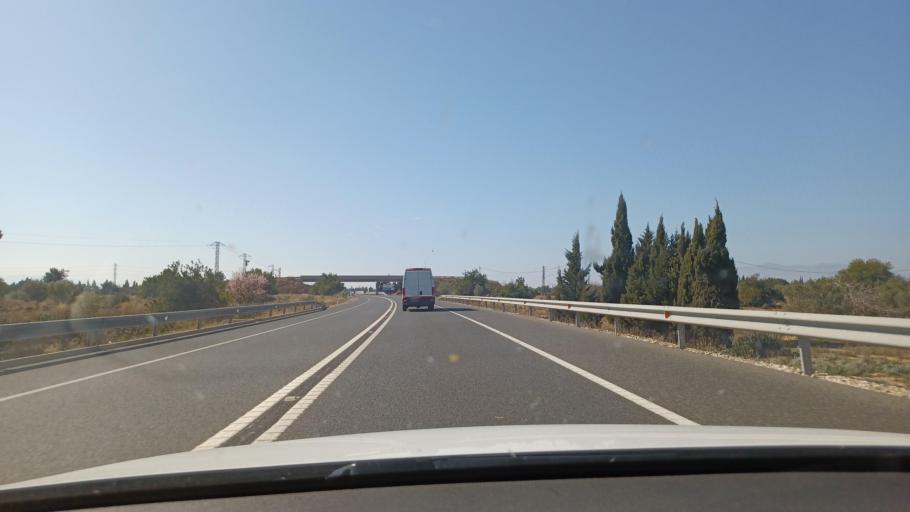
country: ES
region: Catalonia
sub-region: Provincia de Tarragona
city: Camarles
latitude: 40.7593
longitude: 0.6218
